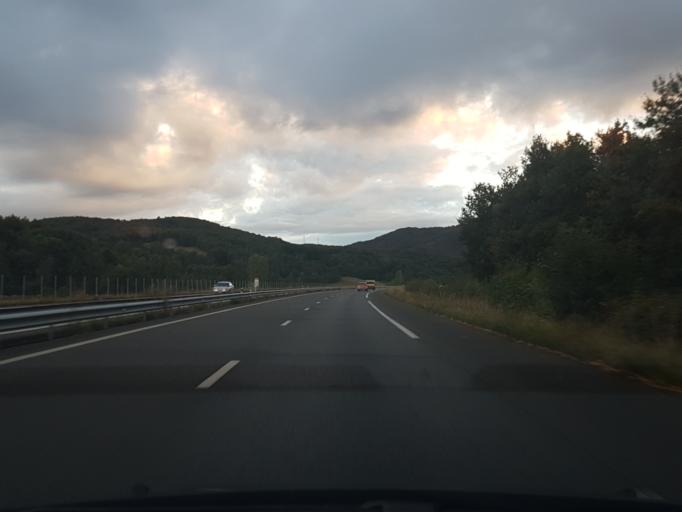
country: FR
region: Midi-Pyrenees
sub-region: Departement de l'Ariege
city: Varilhes
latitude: 43.0516
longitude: 1.6493
